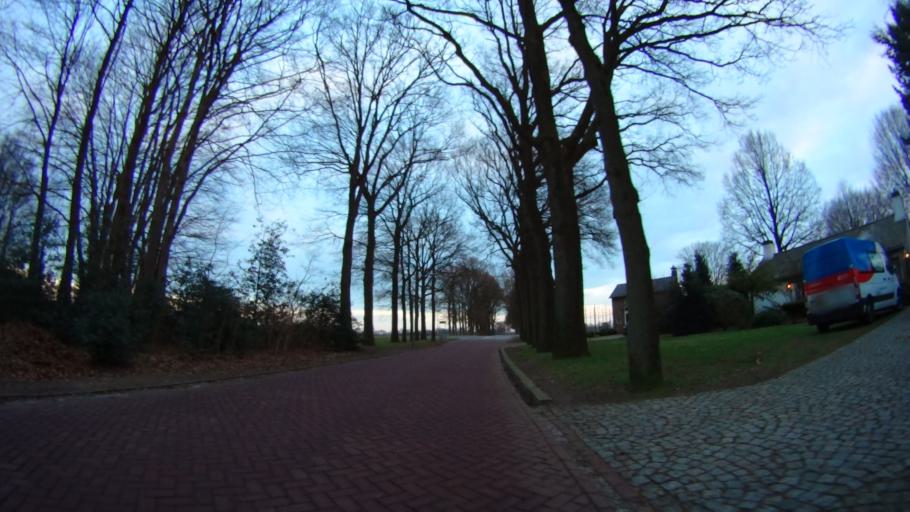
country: NL
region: Drenthe
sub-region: Gemeente Coevorden
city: Sleen
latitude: 52.7744
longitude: 6.8063
